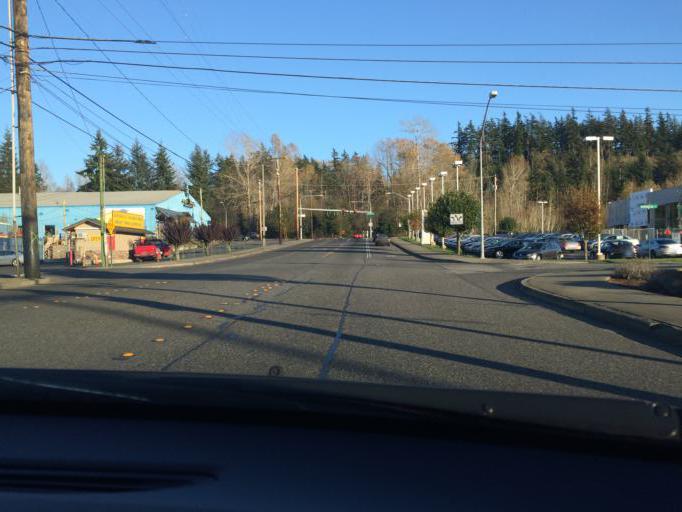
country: US
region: Washington
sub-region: Whatcom County
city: Bellingham
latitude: 48.7564
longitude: -122.4470
